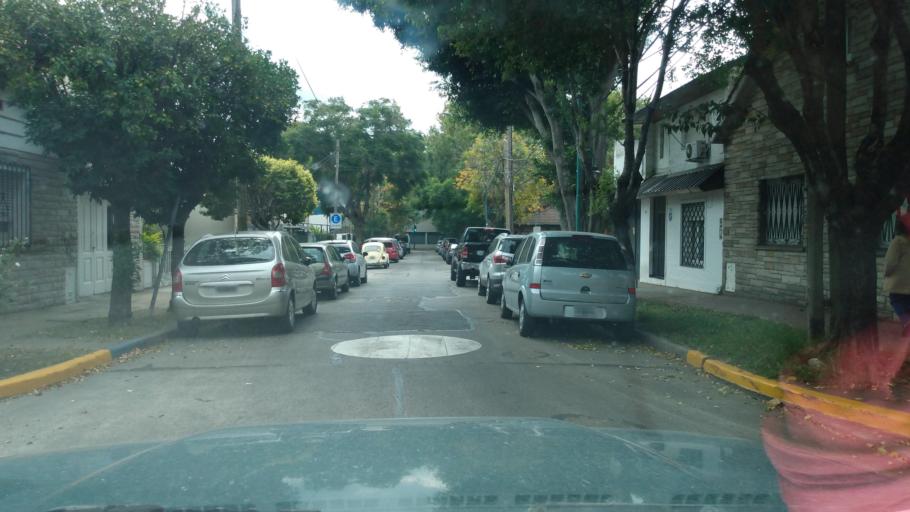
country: AR
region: Buenos Aires
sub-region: Partido de Vicente Lopez
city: Olivos
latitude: -34.5115
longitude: -58.4970
